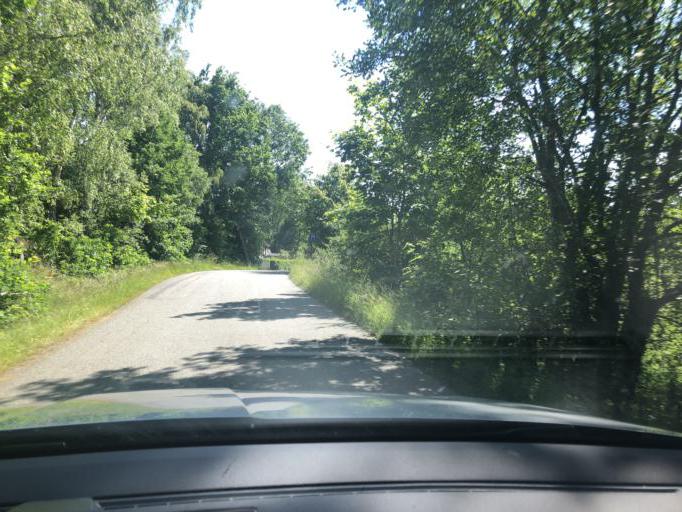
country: SE
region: Blekinge
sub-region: Karlshamns Kommun
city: Morrum
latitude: 56.1634
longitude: 14.8028
